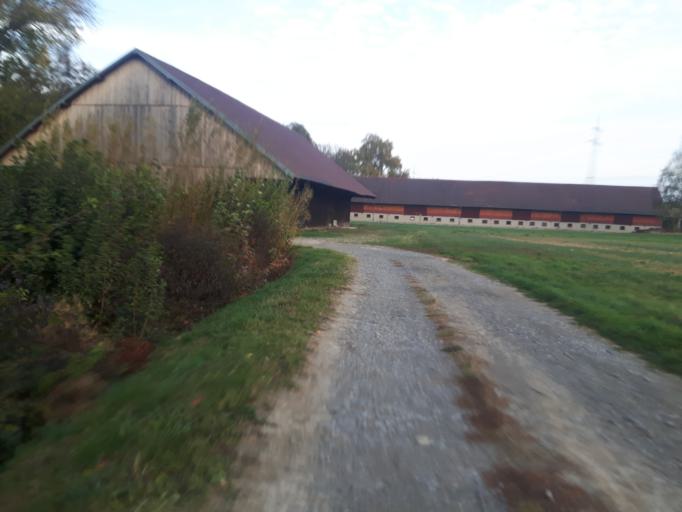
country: DE
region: Baden-Wuerttemberg
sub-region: Regierungsbezirk Stuttgart
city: Leingarten
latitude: 49.1589
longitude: 9.1444
